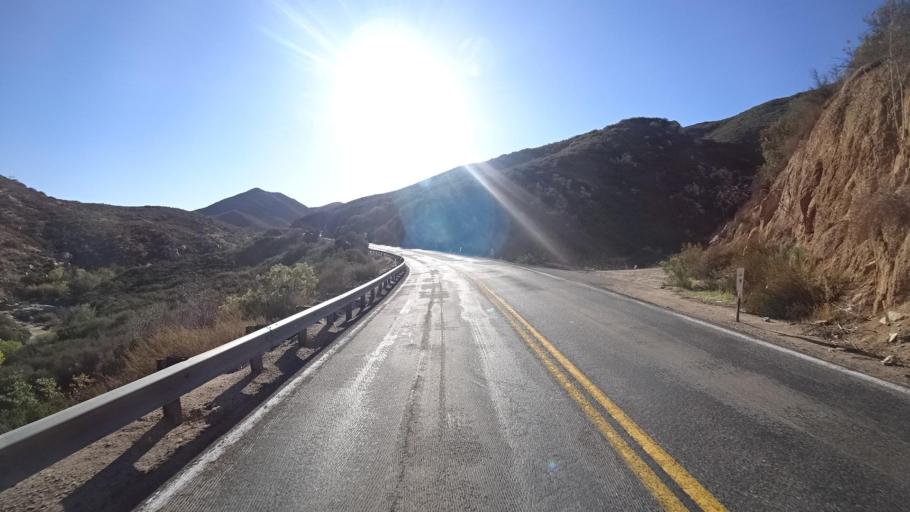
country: MX
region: Baja California
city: Tecate
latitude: 32.5953
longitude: -116.6728
